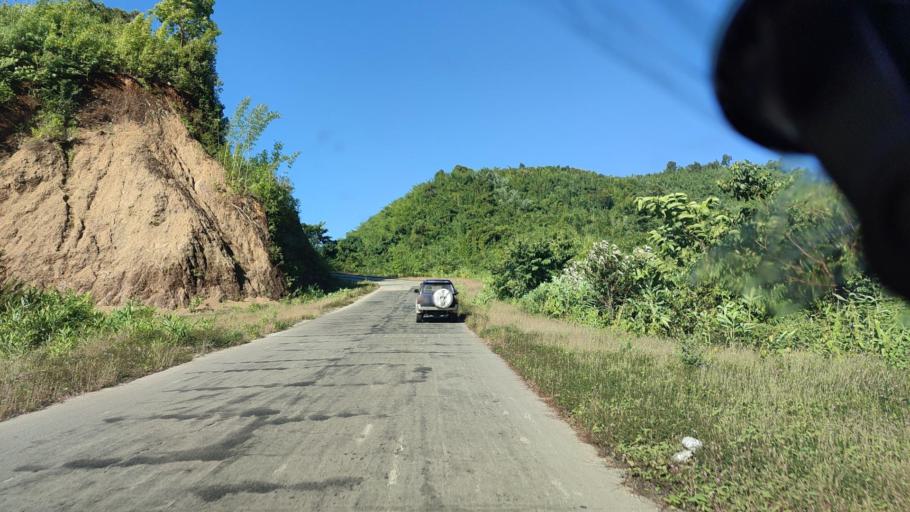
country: MM
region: Rakhine
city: Sittwe
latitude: 19.9313
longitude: 93.7724
